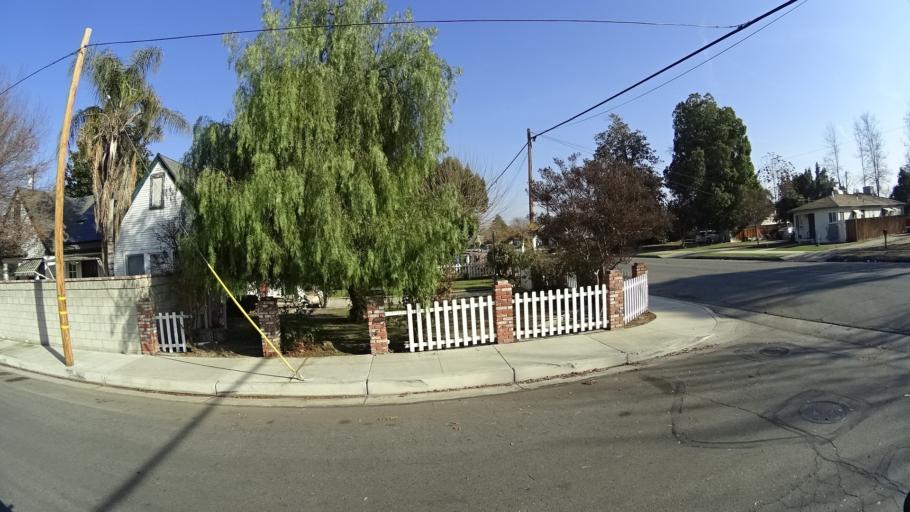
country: US
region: California
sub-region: Kern County
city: Bakersfield
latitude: 35.3652
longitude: -119.0341
